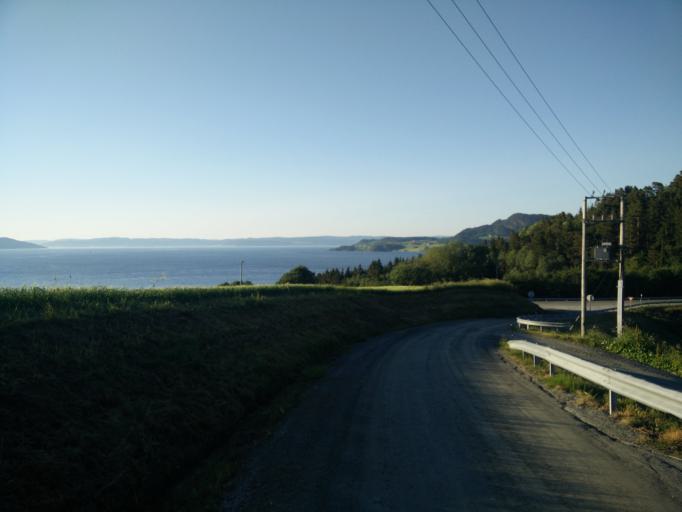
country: NO
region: Sor-Trondelag
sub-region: Skaun
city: Borsa
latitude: 63.3452
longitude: 10.0405
